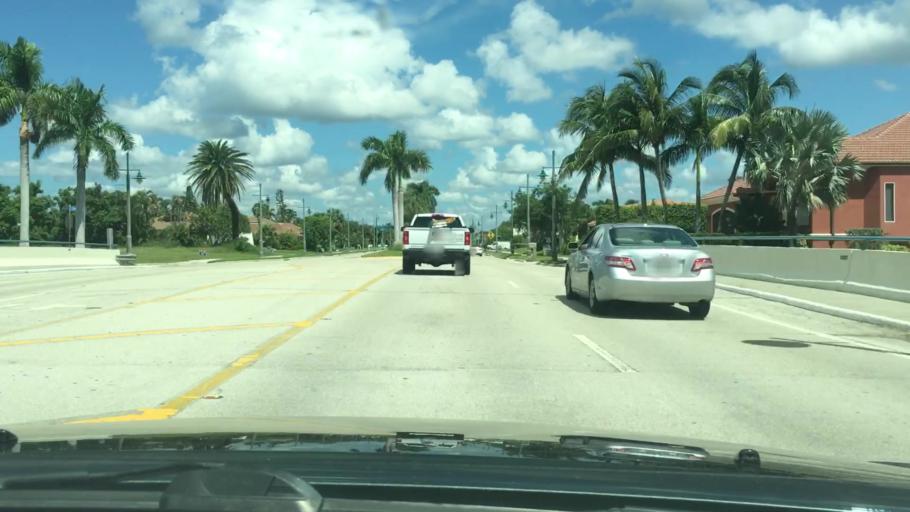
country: US
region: Florida
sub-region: Collier County
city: Marco
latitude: 25.9454
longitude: -81.7325
